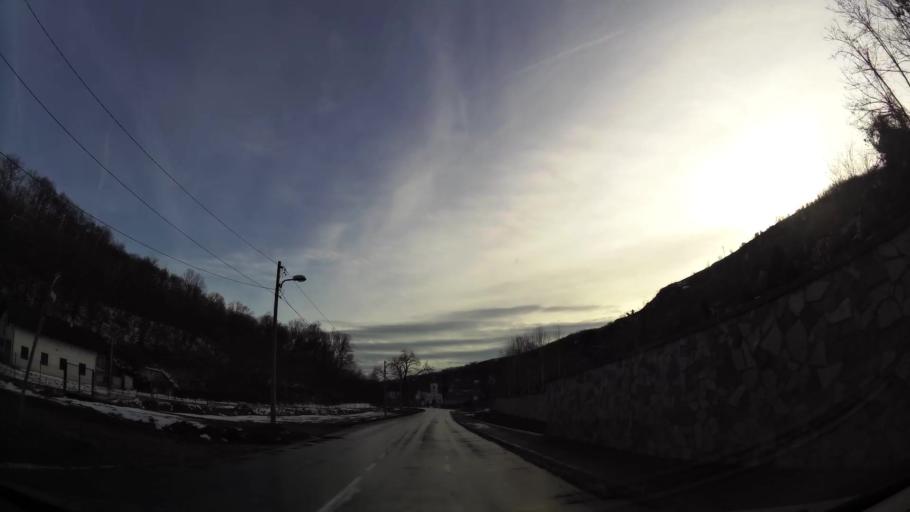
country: RS
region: Central Serbia
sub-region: Belgrade
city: Rakovica
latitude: 44.7336
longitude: 20.4470
